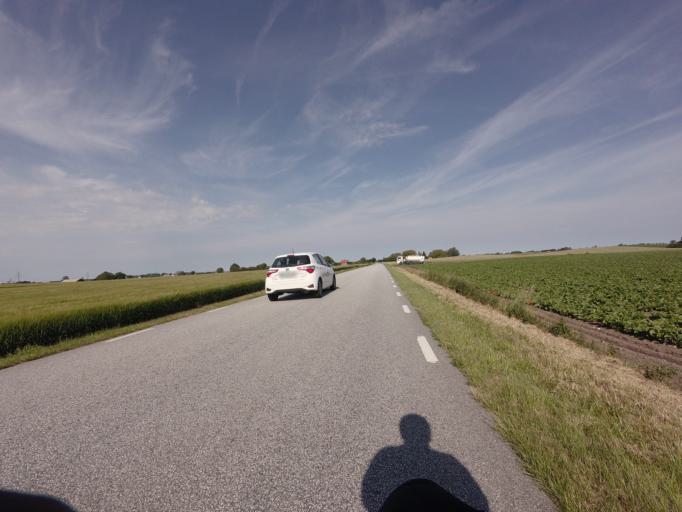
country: SE
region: Skane
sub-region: Malmo
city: Oxie
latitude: 55.4939
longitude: 13.0889
